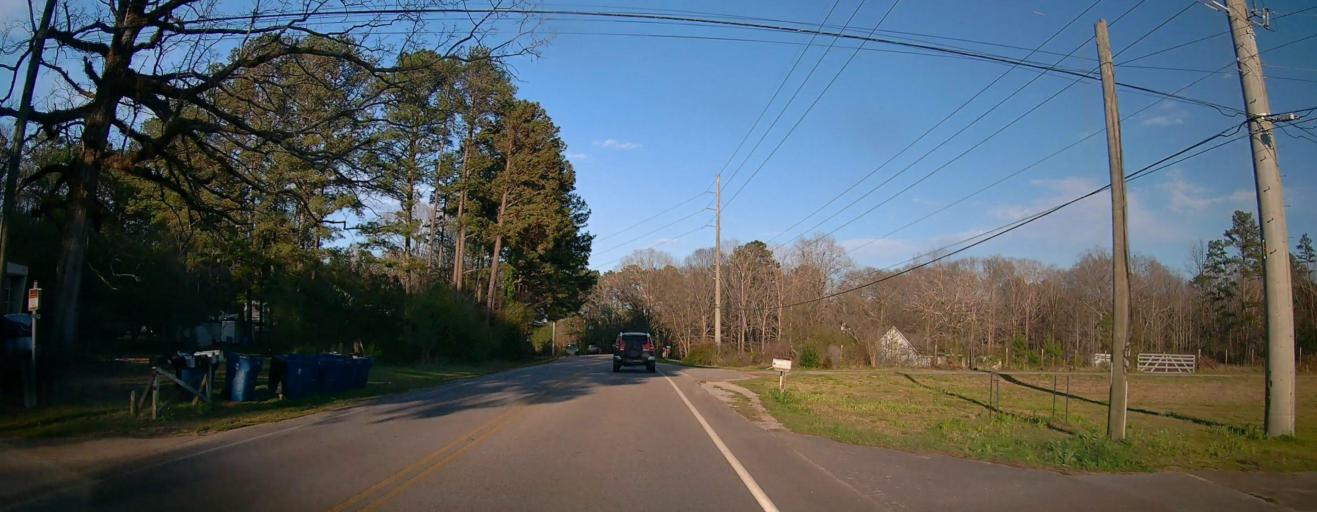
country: US
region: Alabama
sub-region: Shelby County
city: Indian Springs Village
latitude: 33.3277
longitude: -86.6974
